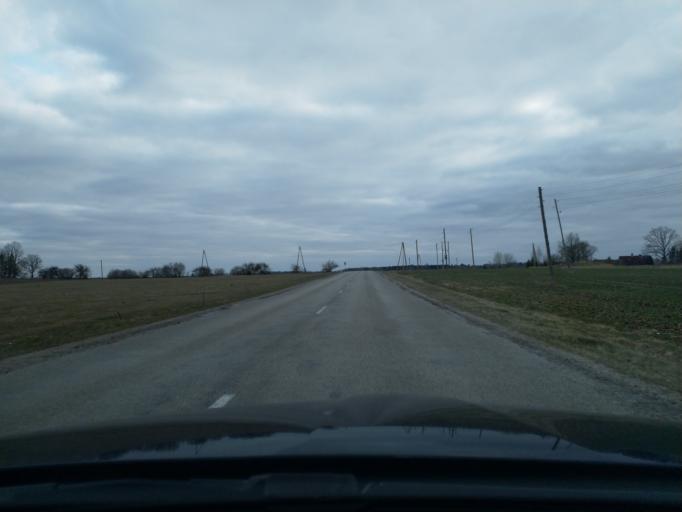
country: LV
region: Talsu Rajons
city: Sabile
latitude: 56.9476
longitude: 22.6038
